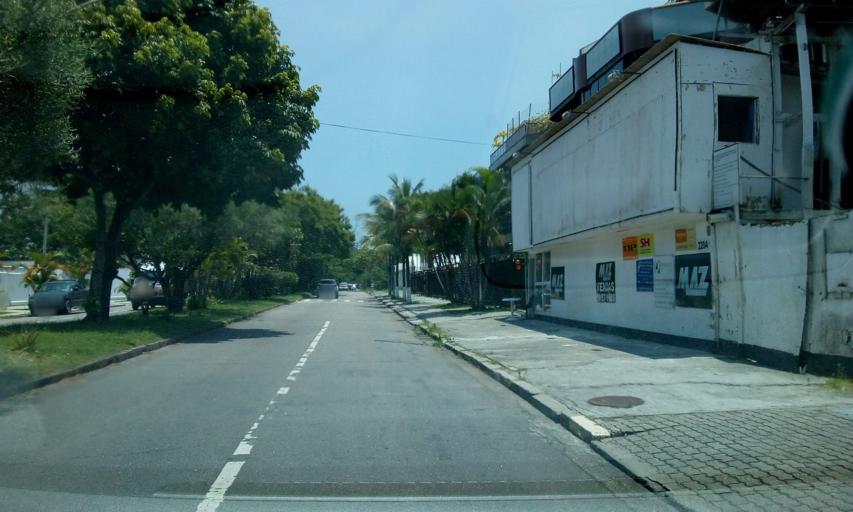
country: BR
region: Rio de Janeiro
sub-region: Nilopolis
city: Nilopolis
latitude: -23.0186
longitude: -43.4670
